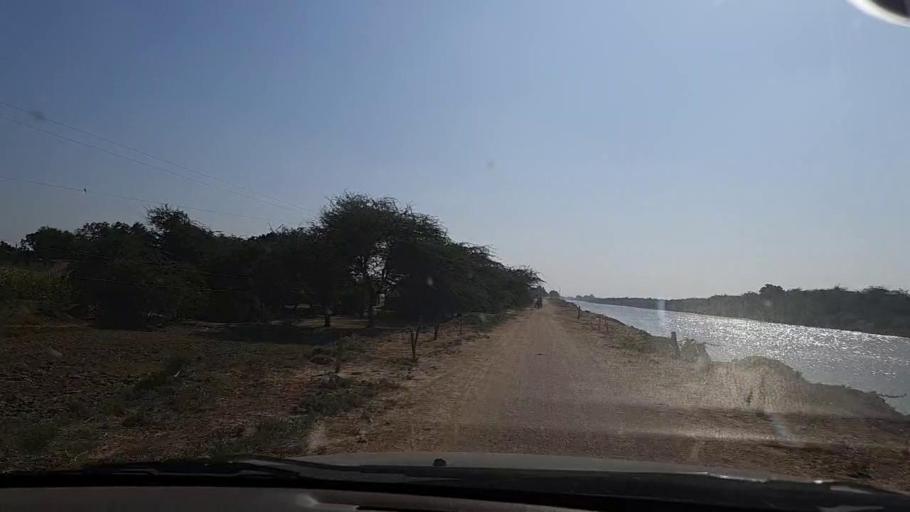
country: PK
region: Sindh
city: Thatta
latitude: 24.6023
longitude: 68.0507
